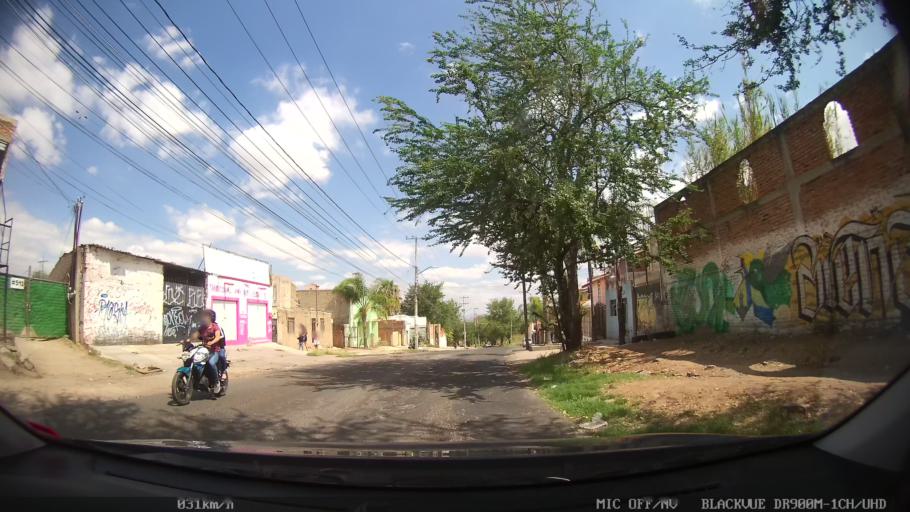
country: MX
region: Jalisco
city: Tonala
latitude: 20.6341
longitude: -103.2513
